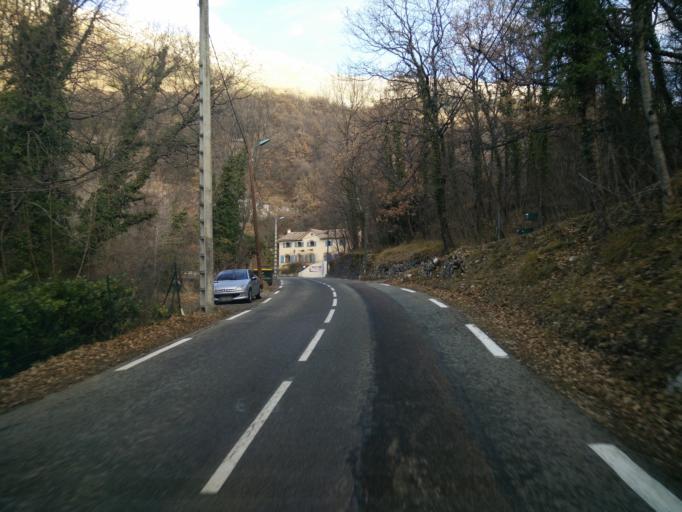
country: FR
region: Provence-Alpes-Cote d'Azur
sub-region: Departement des Alpes-Maritimes
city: Tourrettes-sur-Loup
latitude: 43.7929
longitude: 6.9743
